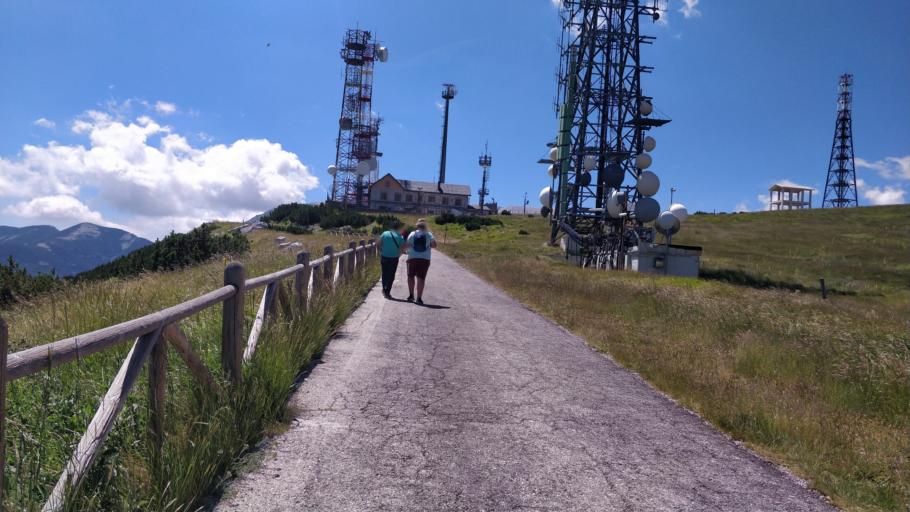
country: IT
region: Abruzzo
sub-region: Provincia di Chieti
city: Pretoro
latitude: 42.1604
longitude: 14.1328
